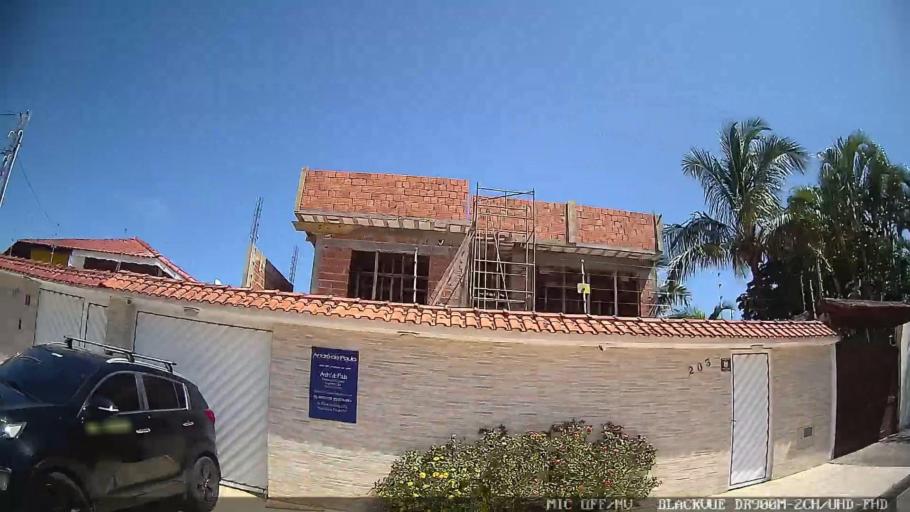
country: BR
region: Sao Paulo
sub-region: Peruibe
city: Peruibe
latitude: -24.2976
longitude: -46.9798
